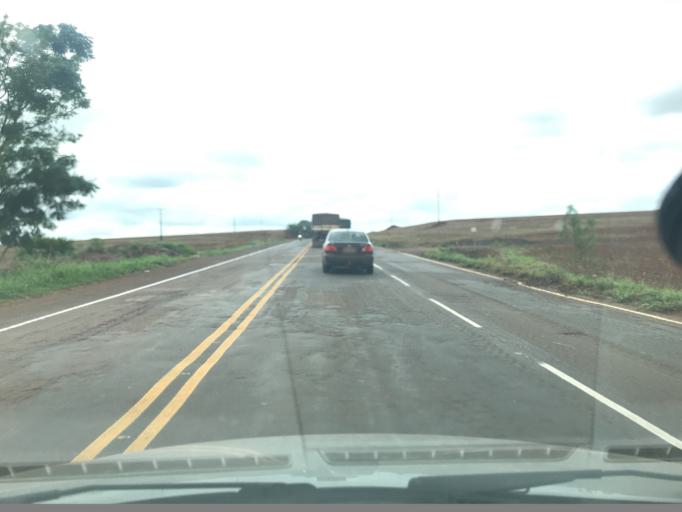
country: BR
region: Parana
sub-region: Terra Boa
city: Terra Boa
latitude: -23.6134
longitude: -52.4272
